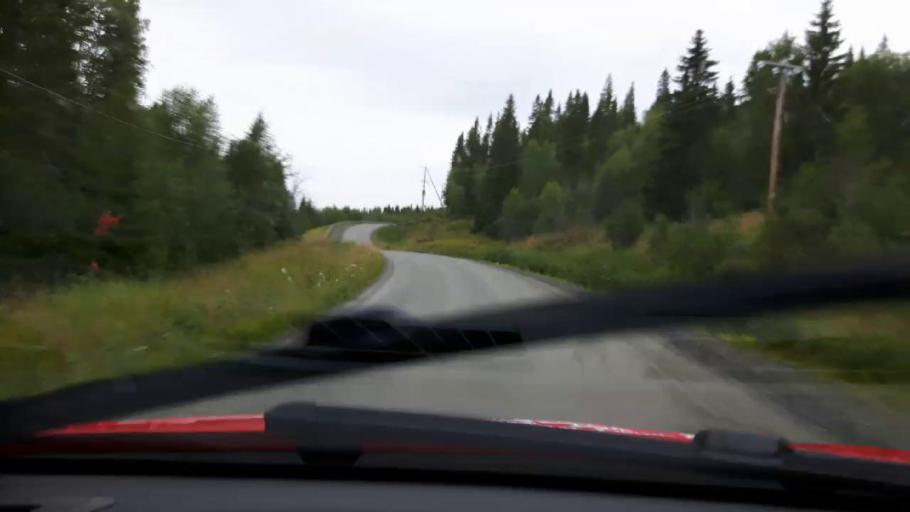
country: SE
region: Jaemtland
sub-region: Are Kommun
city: Are
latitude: 63.4023
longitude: 12.8395
